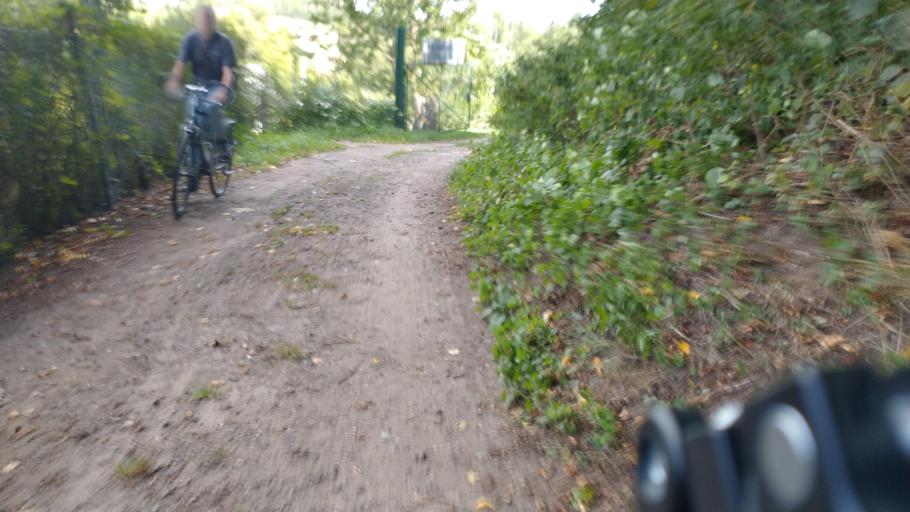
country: DE
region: Schleswig-Holstein
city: Bad Oldesloe
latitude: 53.8149
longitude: 10.3586
